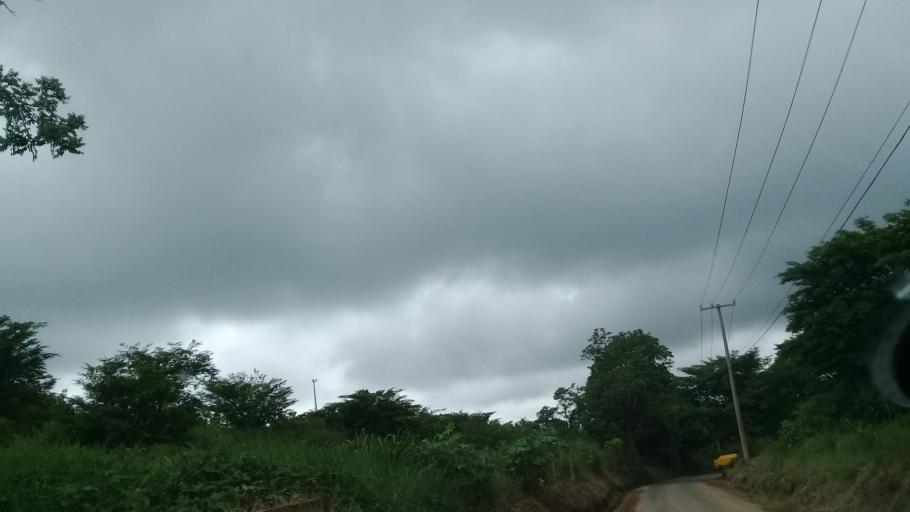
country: MX
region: Veracruz
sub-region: Xalapa
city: Colonia Santa Barbara
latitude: 19.4949
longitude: -96.8713
